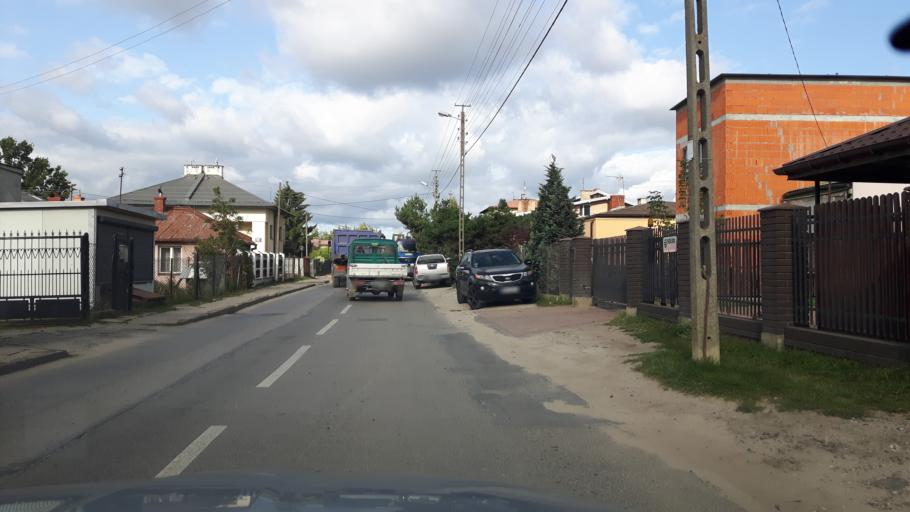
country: PL
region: Masovian Voivodeship
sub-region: Powiat wolominski
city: Marki
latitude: 52.3212
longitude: 21.1169
